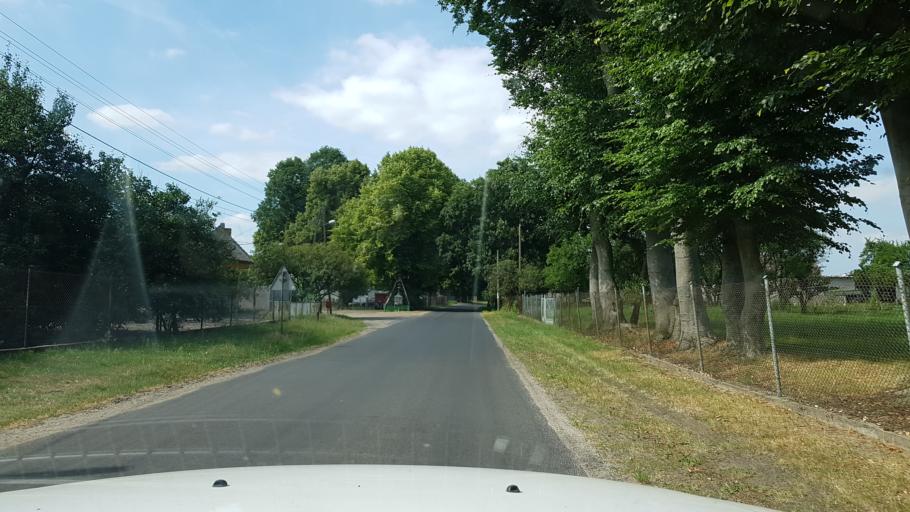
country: PL
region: West Pomeranian Voivodeship
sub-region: Powiat goleniowski
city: Mosty
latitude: 53.5624
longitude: 14.9754
